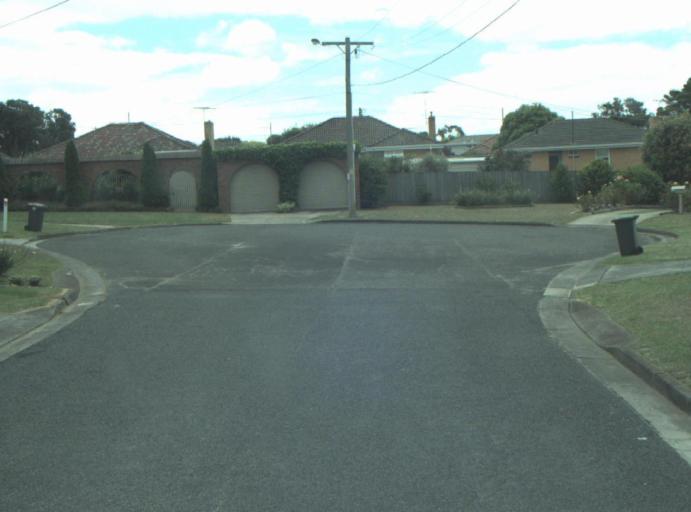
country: AU
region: Victoria
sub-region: Greater Geelong
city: Wandana Heights
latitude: -38.1829
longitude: 144.3188
